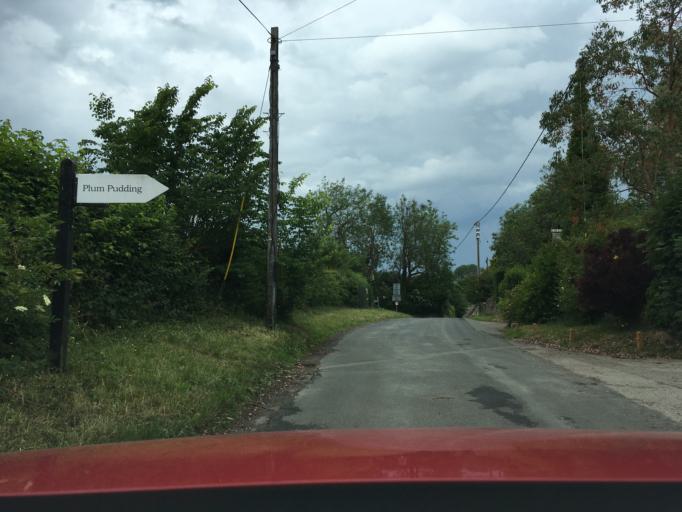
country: GB
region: England
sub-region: Gloucestershire
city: Shurdington
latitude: 51.8103
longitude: -2.0889
